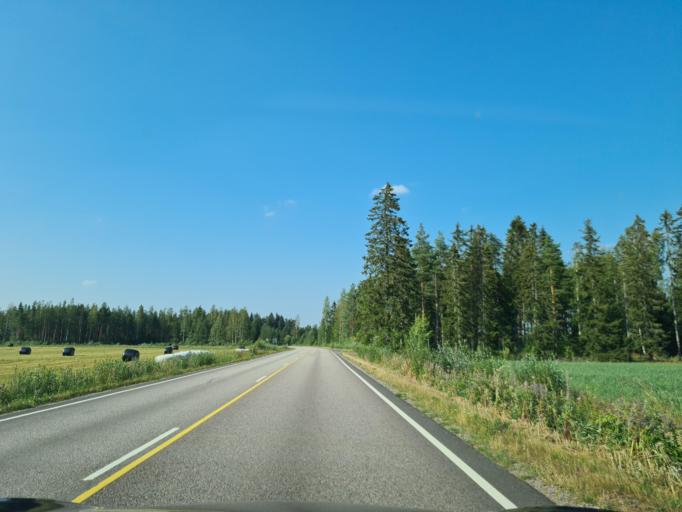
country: FI
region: Satakunta
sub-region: Pohjois-Satakunta
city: Karvia
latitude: 62.1893
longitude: 22.5968
